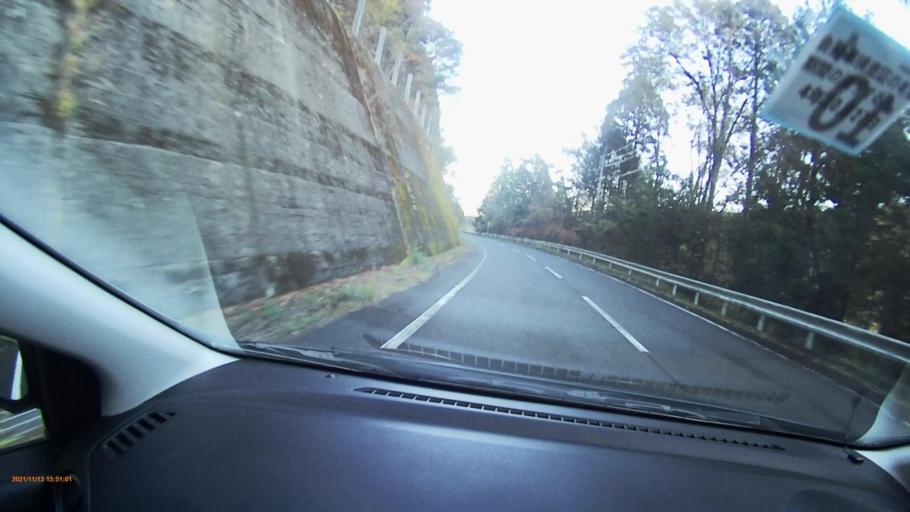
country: JP
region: Gifu
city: Nakatsugawa
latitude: 35.5970
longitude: 137.4170
